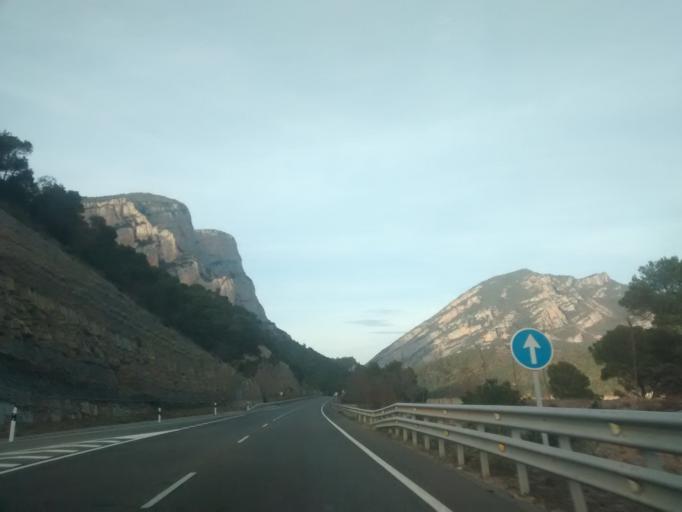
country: ES
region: Catalonia
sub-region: Provincia de Lleida
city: Oliana
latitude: 42.1079
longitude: 1.2996
